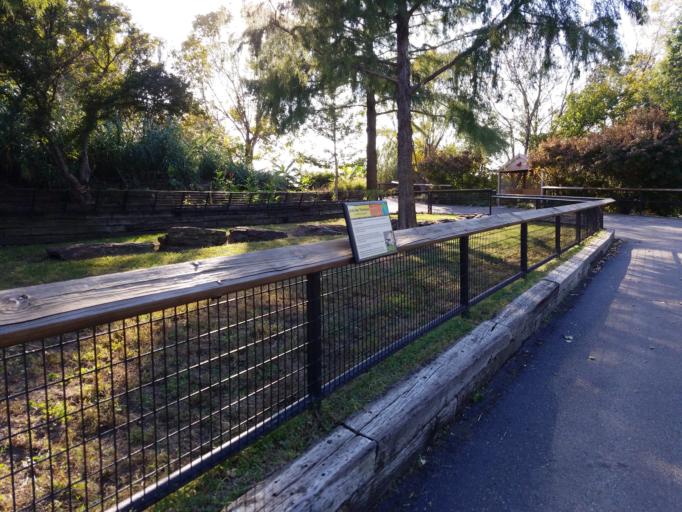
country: US
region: Kansas
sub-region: Saline County
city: Salina
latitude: 38.8553
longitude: -97.7623
